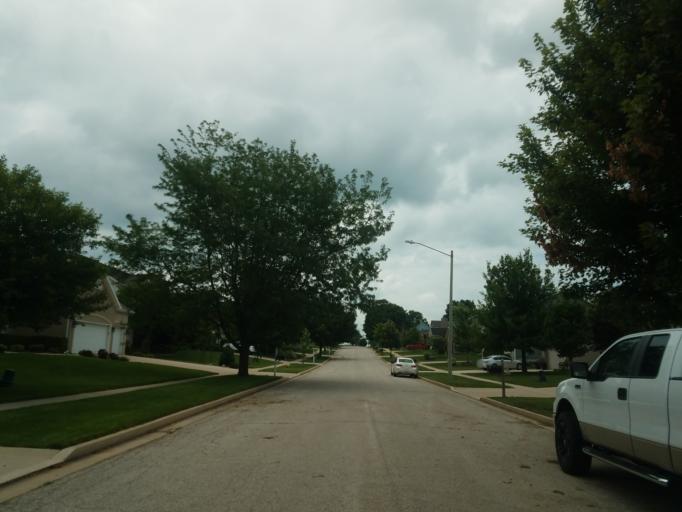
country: US
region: Illinois
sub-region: McLean County
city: Twin Grove
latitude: 40.4495
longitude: -89.0480
